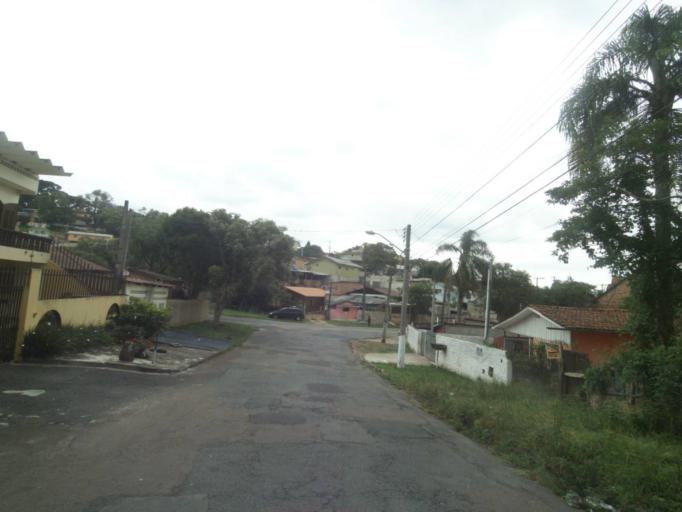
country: BR
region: Parana
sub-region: Curitiba
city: Curitiba
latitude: -25.3861
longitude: -49.2900
